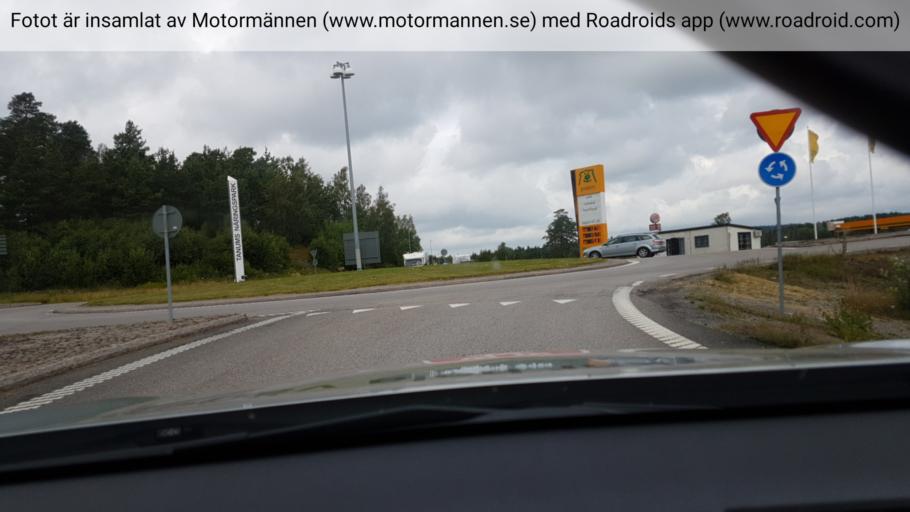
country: SE
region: Vaestra Goetaland
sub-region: Tanums Kommun
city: Tanumshede
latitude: 58.7195
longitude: 11.3505
